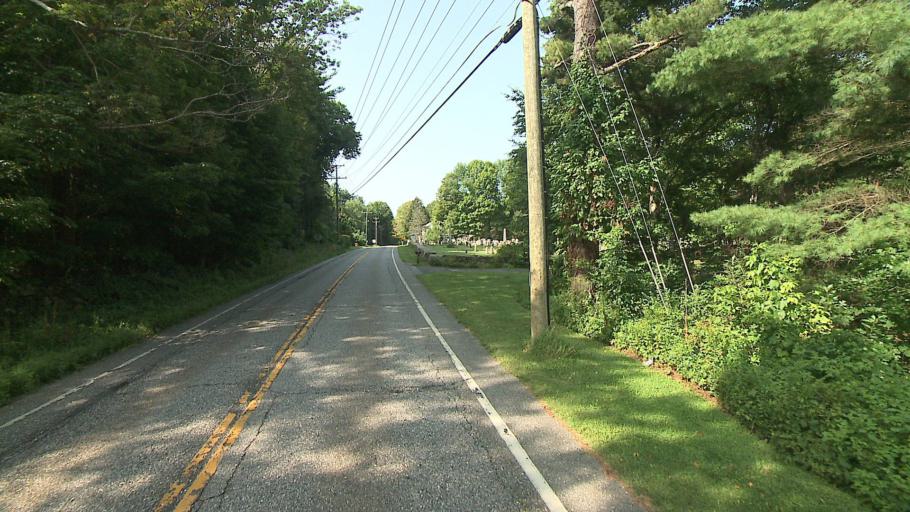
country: US
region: Connecticut
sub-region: Litchfield County
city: Kent
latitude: 41.8050
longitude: -73.3826
